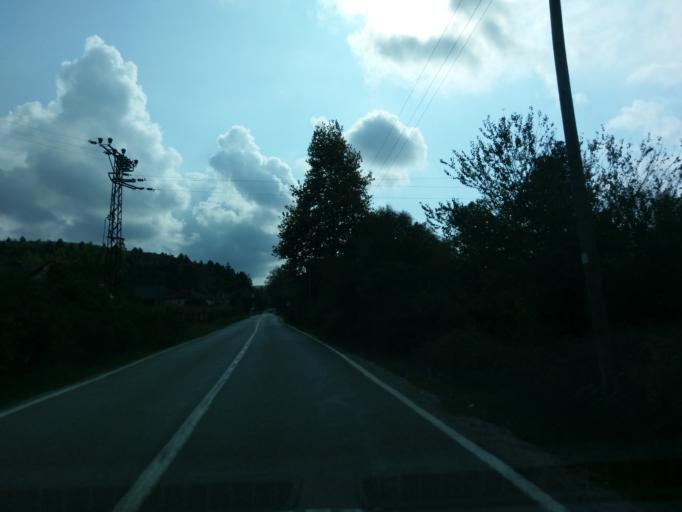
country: TR
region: Sinop
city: Helaldi
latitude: 41.9016
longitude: 34.4546
